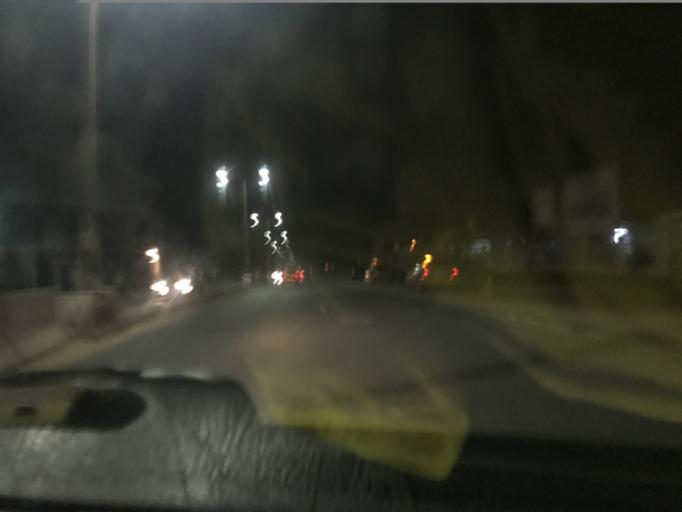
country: SN
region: Dakar
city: Mermoz Boabab
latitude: 14.6950
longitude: -17.4643
